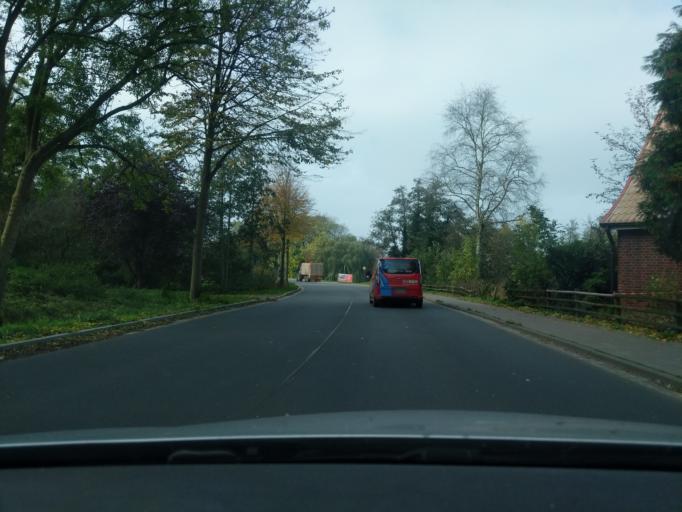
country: DE
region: Lower Saxony
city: Belum
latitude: 53.8174
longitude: 8.9928
